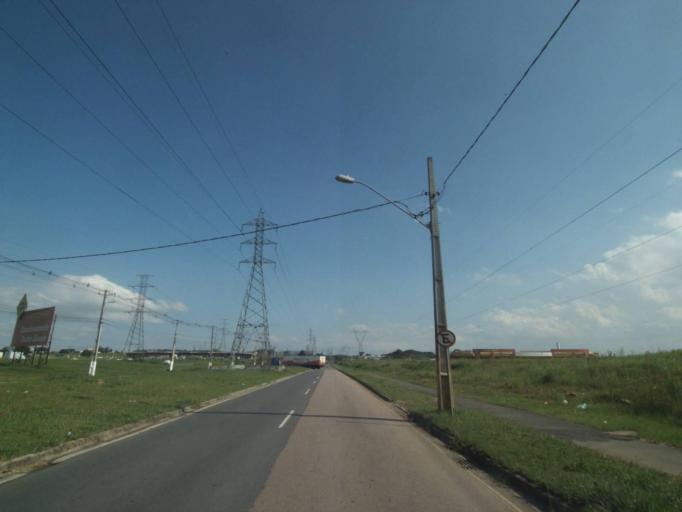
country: BR
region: Parana
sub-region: Araucaria
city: Araucaria
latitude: -25.5188
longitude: -49.3363
